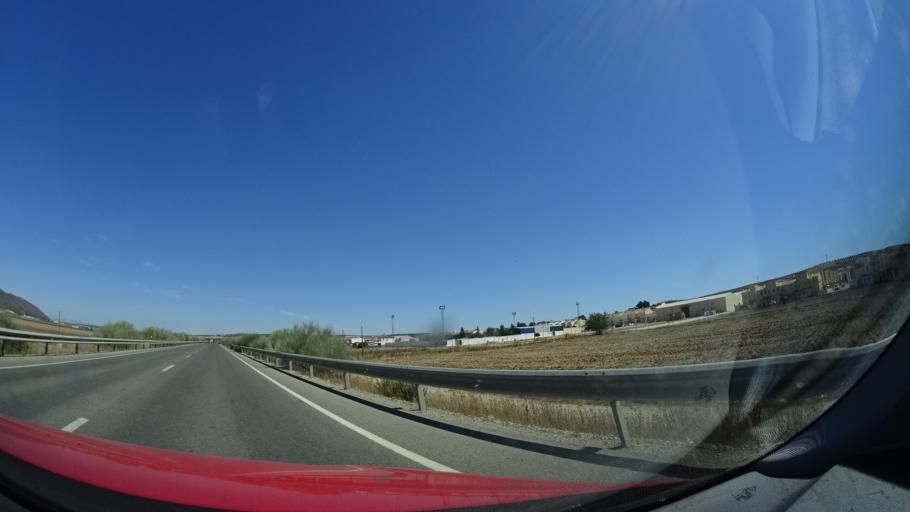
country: ES
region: Andalusia
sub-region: Provincia de Malaga
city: Sierra de Yeguas
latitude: 37.1297
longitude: -4.8706
